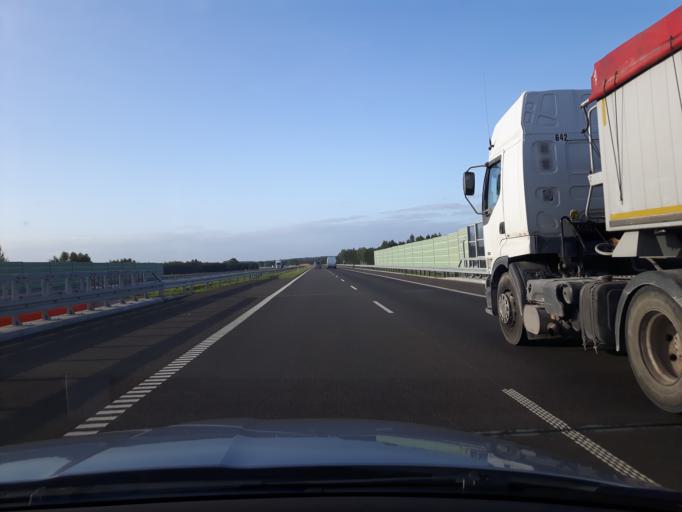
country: PL
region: Masovian Voivodeship
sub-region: Powiat radomski
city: Wolanow
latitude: 51.3713
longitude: 21.0160
